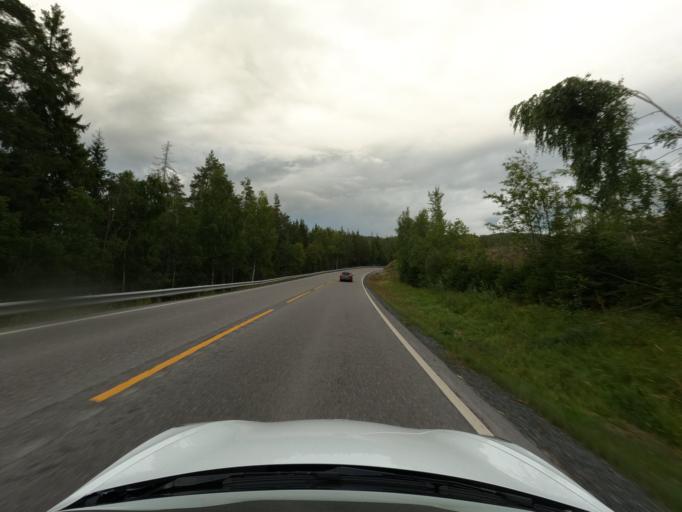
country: NO
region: Telemark
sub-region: Notodden
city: Notodden
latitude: 59.5837
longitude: 9.2997
